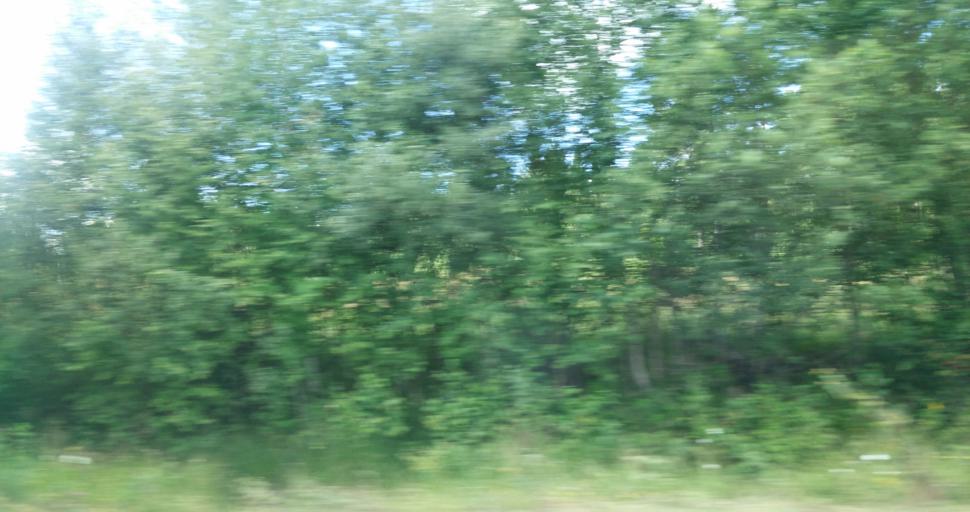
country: SE
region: Vaermland
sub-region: Hagfors Kommun
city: Ekshaerad
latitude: 60.0396
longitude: 13.4969
